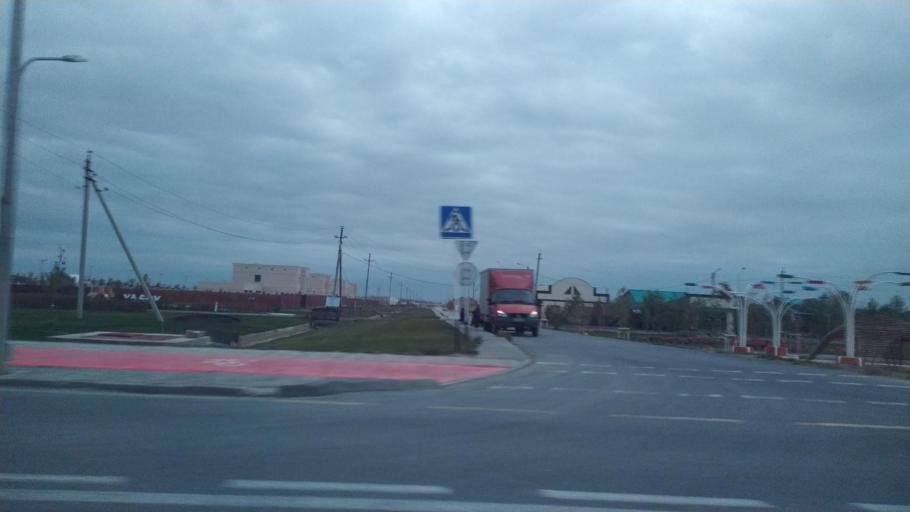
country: KZ
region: Ongtustik Qazaqstan
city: Turkestan
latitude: 43.2771
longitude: 68.3301
